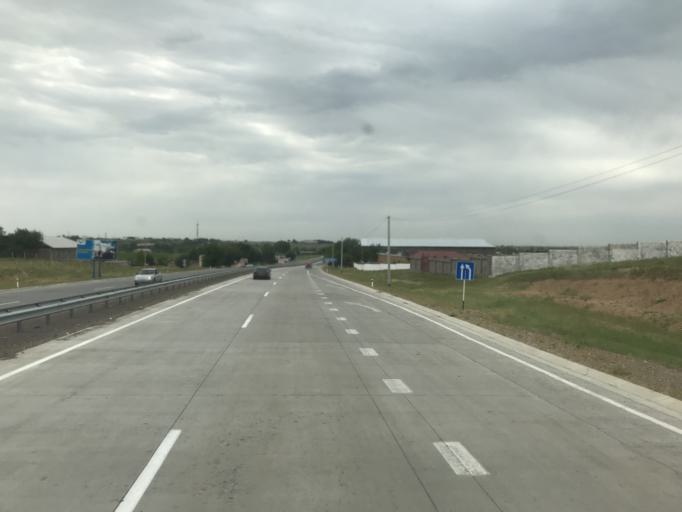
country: UZ
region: Toshkent
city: Salor
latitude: 41.5067
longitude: 69.3745
